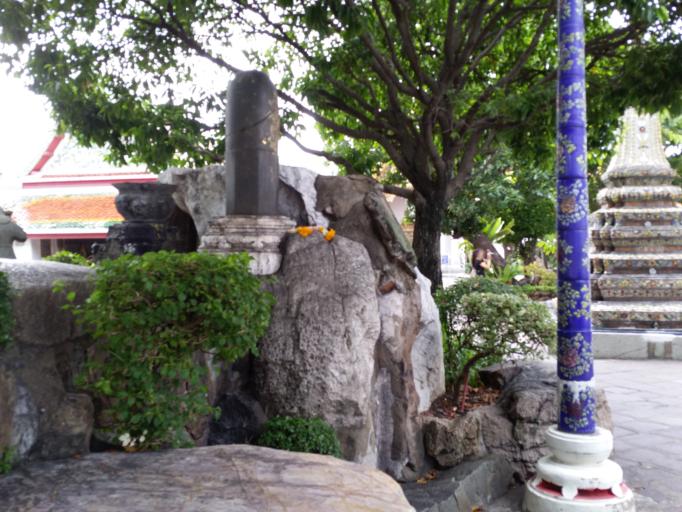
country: TH
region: Bangkok
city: Bangkok
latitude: 13.7463
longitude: 100.4927
